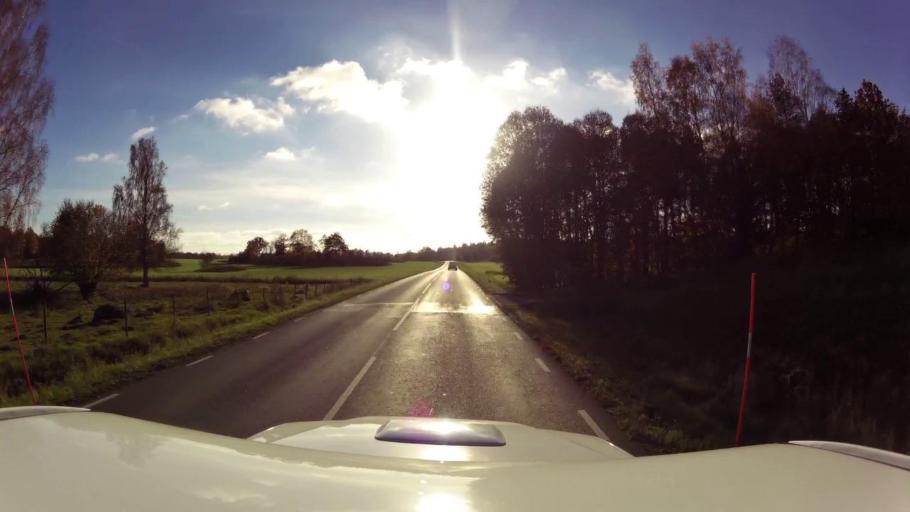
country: SE
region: OEstergoetland
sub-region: Linkopings Kommun
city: Malmslatt
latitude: 58.3395
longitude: 15.5150
